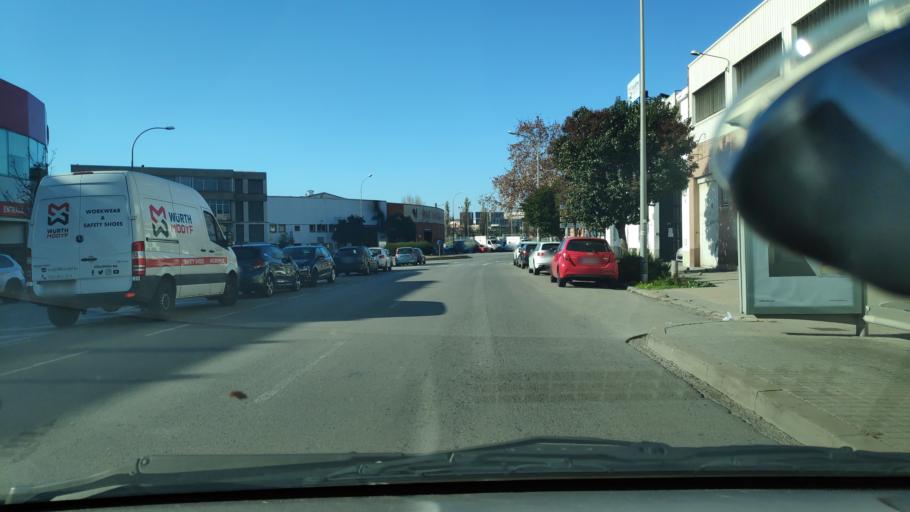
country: ES
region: Catalonia
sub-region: Provincia de Barcelona
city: Sabadell
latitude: 41.5332
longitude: 2.1008
